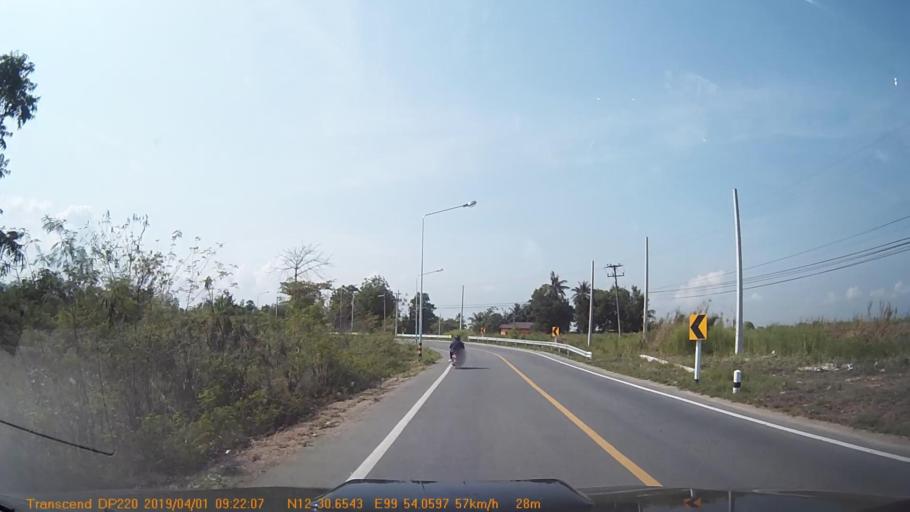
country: TH
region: Prachuap Khiri Khan
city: Hua Hin
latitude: 12.5105
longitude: 99.9010
